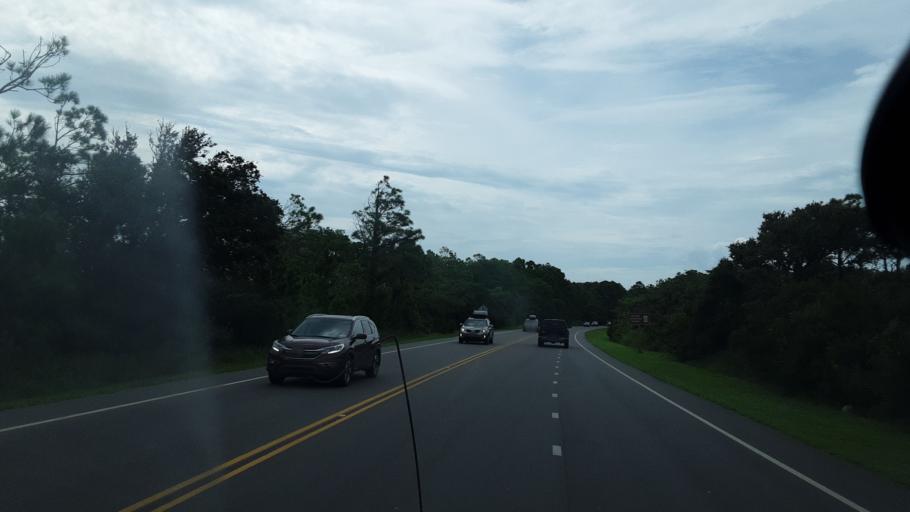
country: US
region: North Carolina
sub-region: Dare County
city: Nags Head
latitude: 35.9037
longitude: -75.5971
